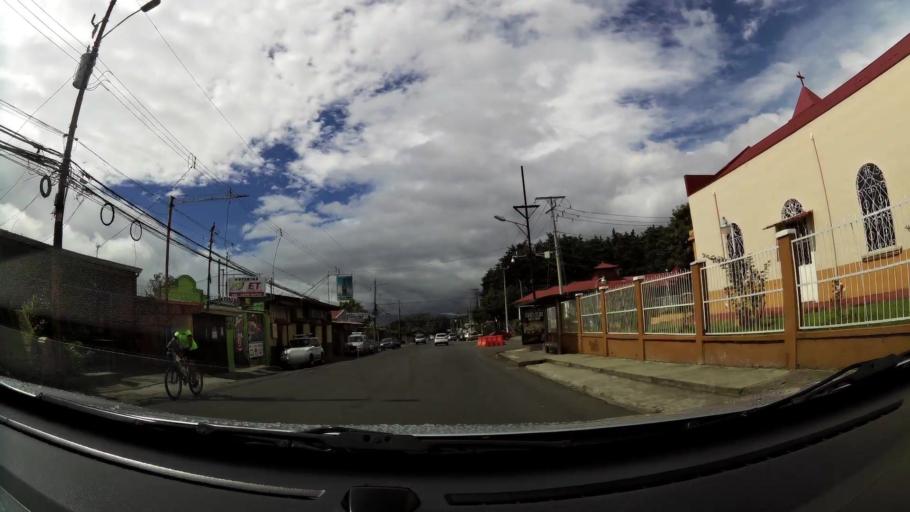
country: CR
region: Cartago
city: Tres Rios
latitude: 9.9079
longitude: -83.9793
